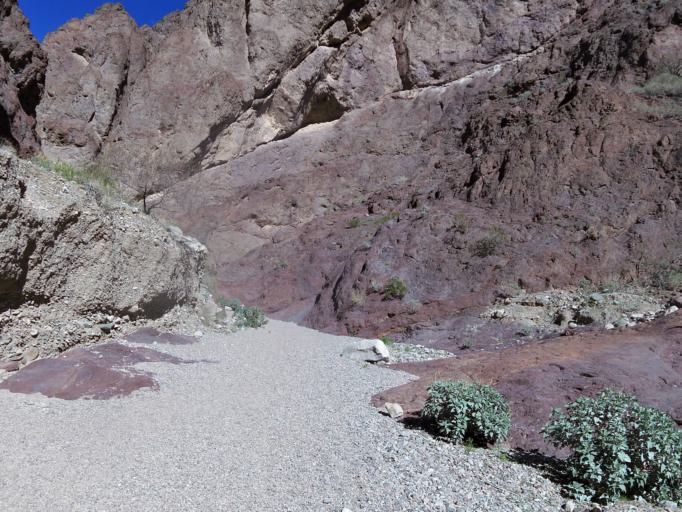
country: US
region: Nevada
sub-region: Clark County
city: Boulder City
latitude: 35.9716
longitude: -114.7163
